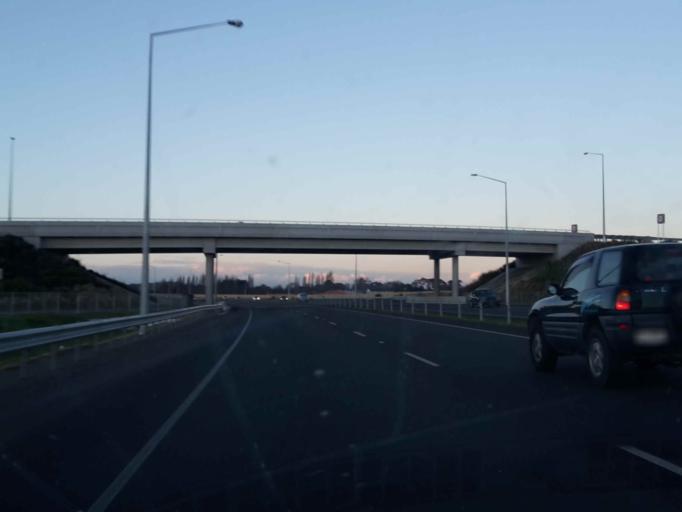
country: NZ
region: Canterbury
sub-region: Selwyn District
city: Prebbleton
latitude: -43.5644
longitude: 172.5523
